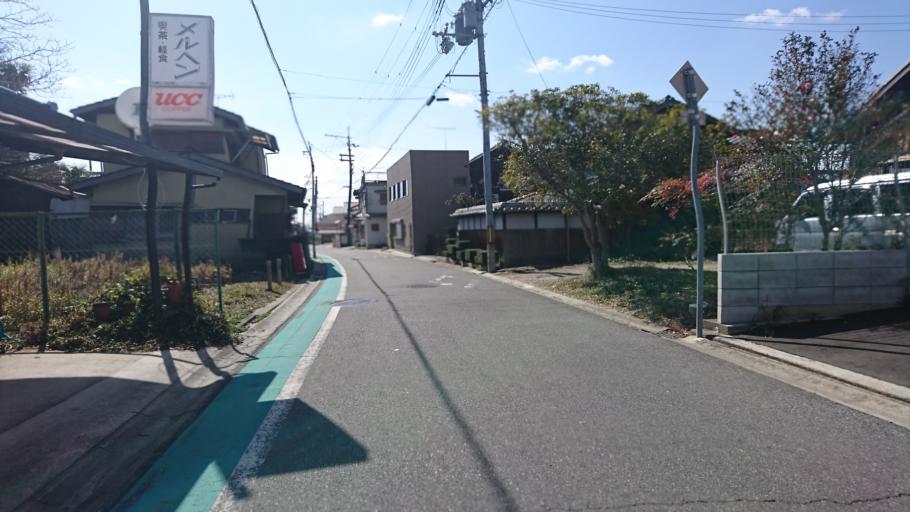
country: JP
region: Hyogo
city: Kakogawacho-honmachi
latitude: 34.8187
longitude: 134.8218
